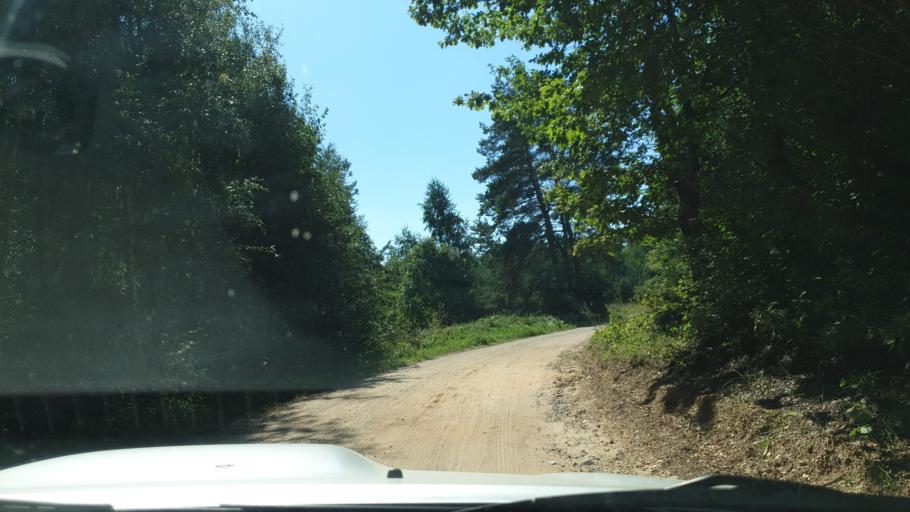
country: LT
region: Vilnius County
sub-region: Vilniaus Rajonas
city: Vievis
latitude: 54.9002
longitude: 24.8768
